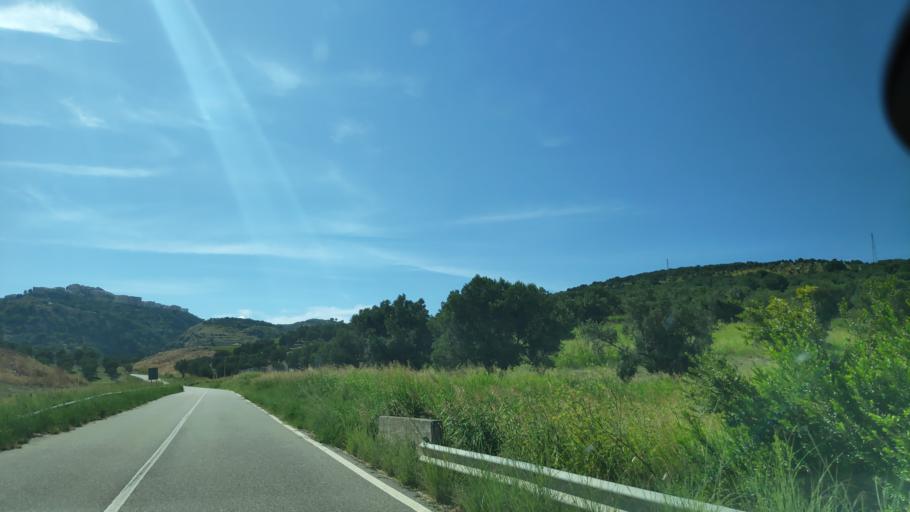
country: IT
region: Calabria
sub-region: Provincia di Catanzaro
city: Staletti
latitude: 38.7846
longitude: 16.5411
